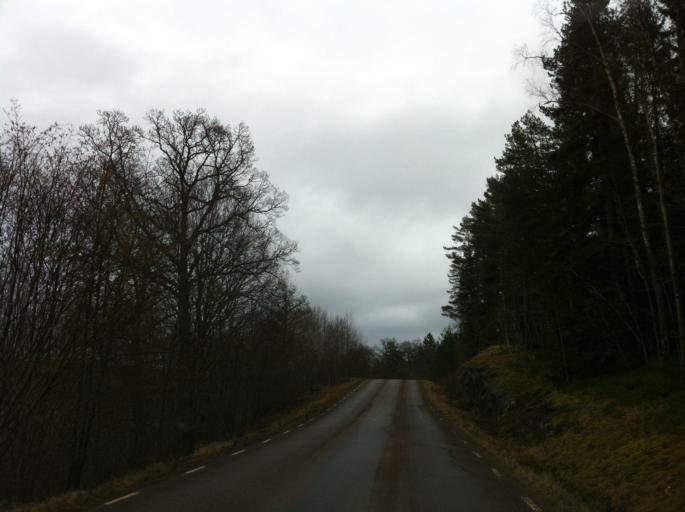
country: SE
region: Kalmar
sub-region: Vasterviks Kommun
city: Vaestervik
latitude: 57.9045
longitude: 16.6984
